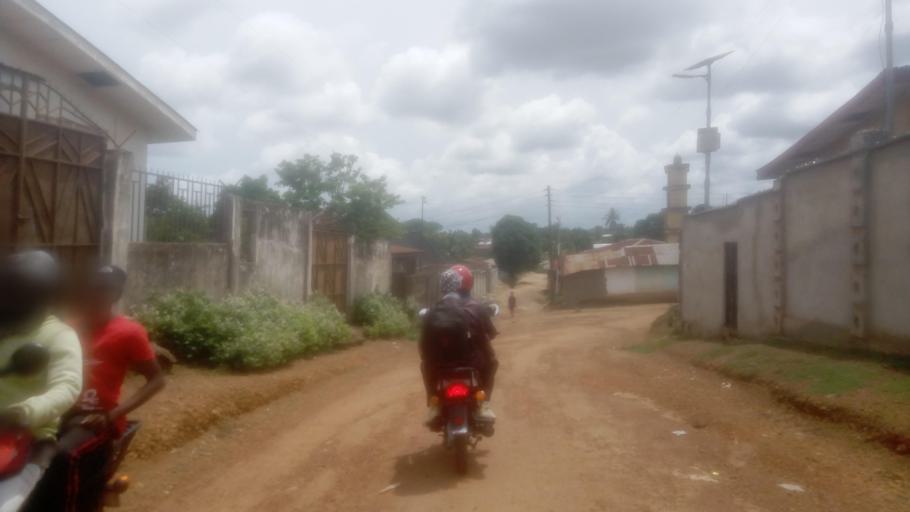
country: SL
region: Southern Province
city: Bo
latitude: 7.9521
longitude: -11.7149
